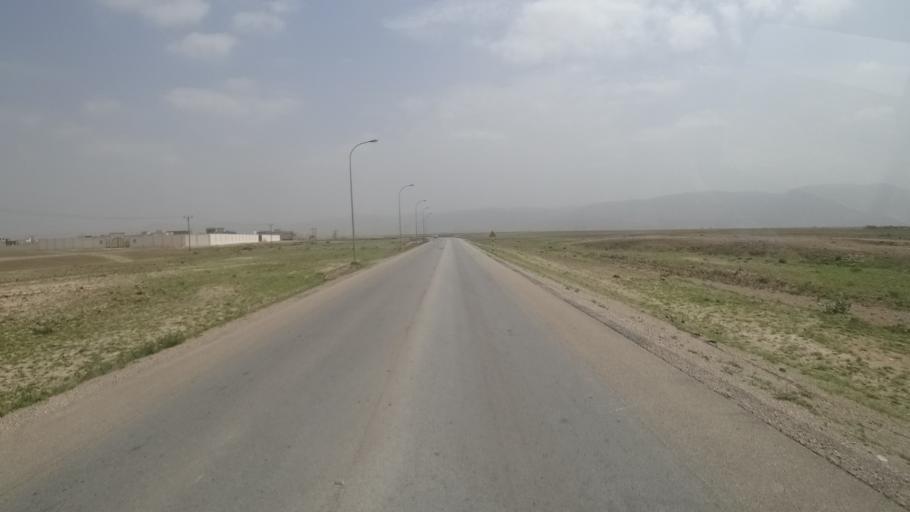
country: OM
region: Zufar
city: Salalah
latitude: 17.0649
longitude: 54.2166
